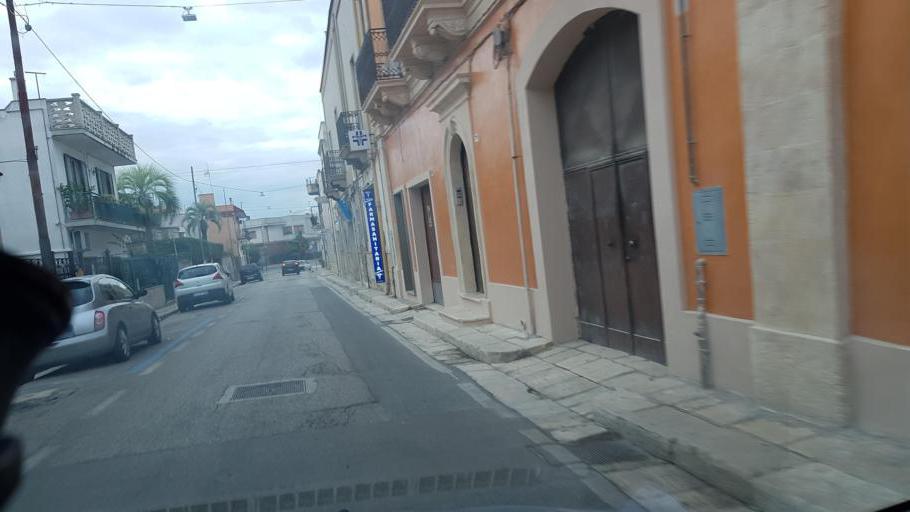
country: IT
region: Apulia
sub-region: Provincia di Brindisi
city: Oria
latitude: 40.5011
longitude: 17.6423
